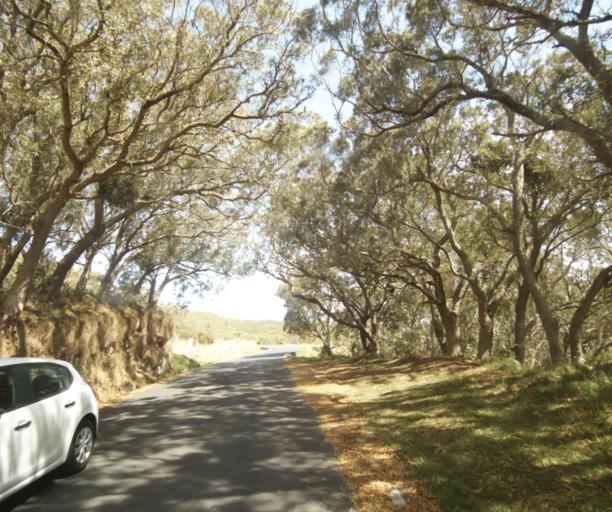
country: RE
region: Reunion
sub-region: Reunion
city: Trois-Bassins
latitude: -21.0598
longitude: 55.3712
